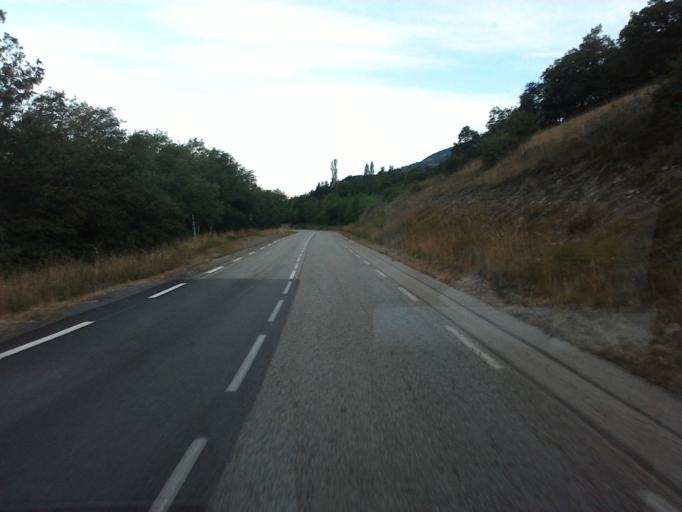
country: FR
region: Rhone-Alpes
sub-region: Departement de l'Isere
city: La Mure
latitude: 44.8242
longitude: 5.9437
